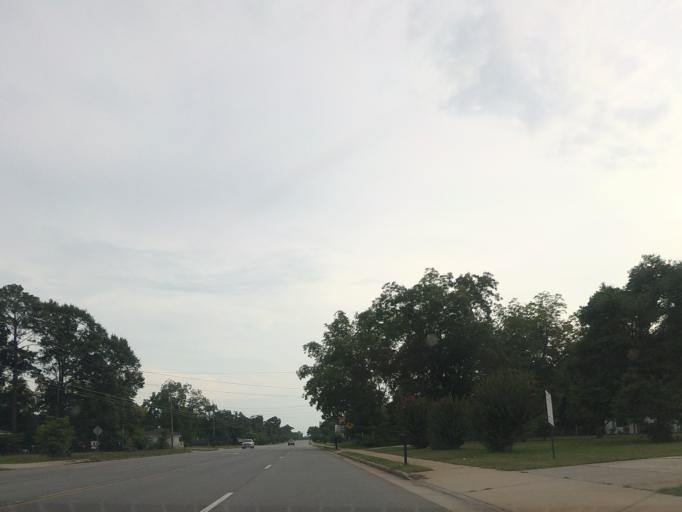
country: US
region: Georgia
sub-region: Bibb County
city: Macon
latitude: 32.7429
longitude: -83.6743
